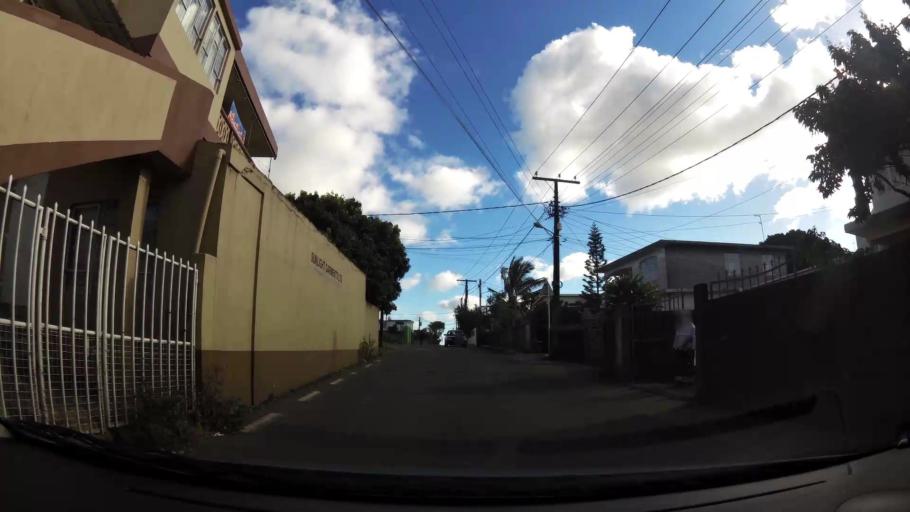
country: MU
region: Plaines Wilhems
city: Curepipe
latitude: -20.2946
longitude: 57.5166
